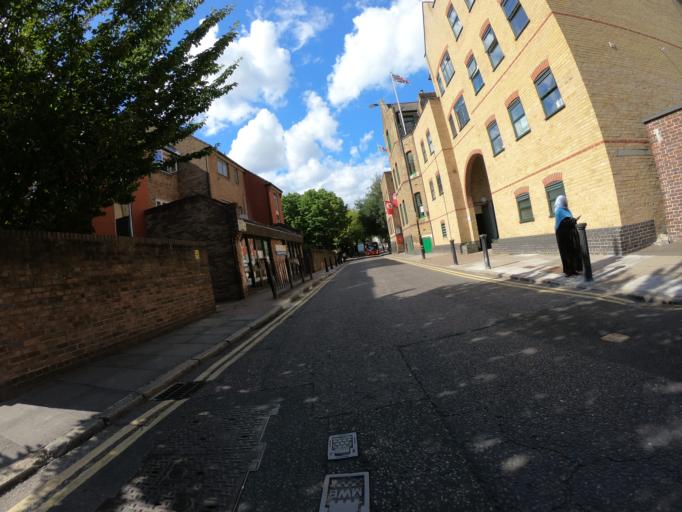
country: GB
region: England
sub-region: Greater London
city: Bethnal Green
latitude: 51.5058
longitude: -0.0585
